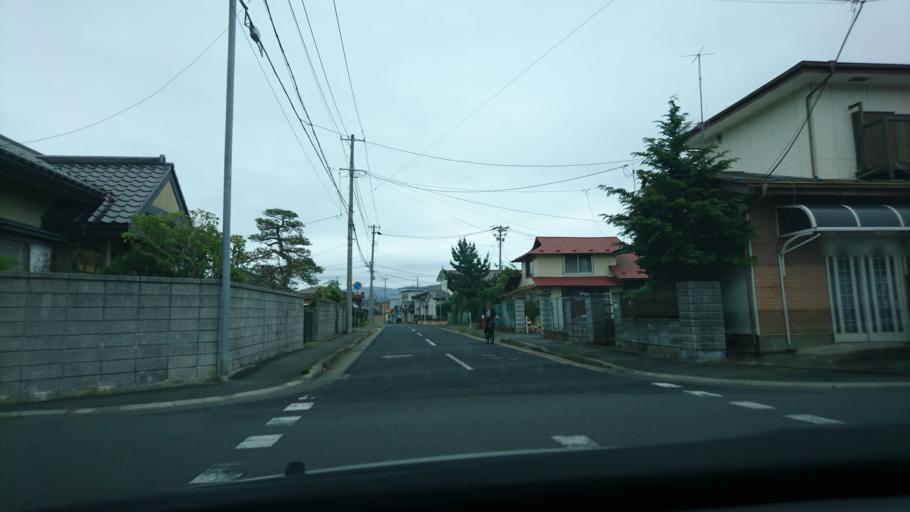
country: JP
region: Iwate
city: Ichinoseki
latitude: 38.9324
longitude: 141.1362
